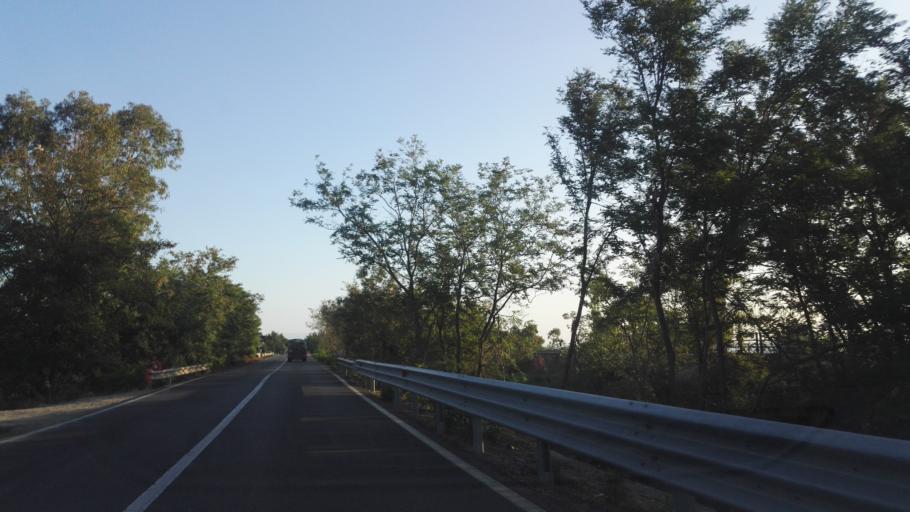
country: IT
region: Calabria
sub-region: Provincia di Catanzaro
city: Santa Caterina dello Ionio Marina
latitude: 38.5495
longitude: 16.5702
